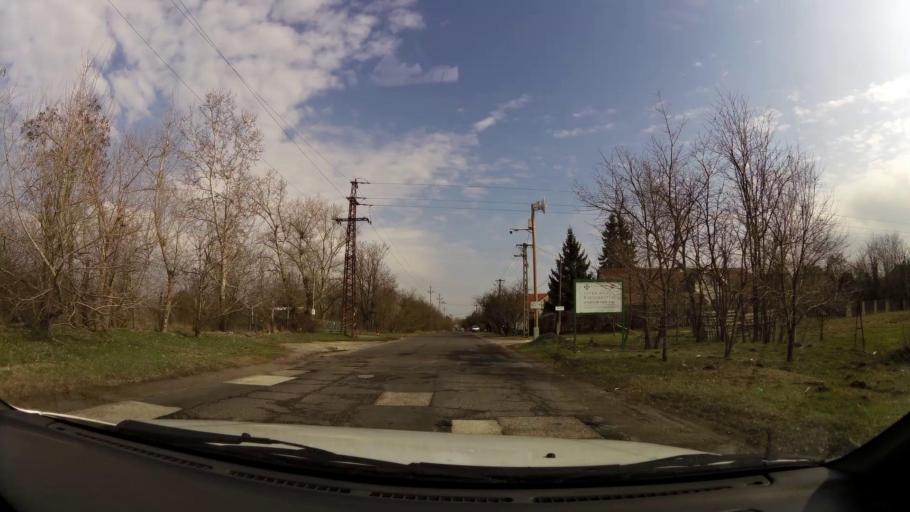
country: HU
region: Budapest
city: Budapest XVII. keruelet
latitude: 47.5039
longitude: 19.2608
